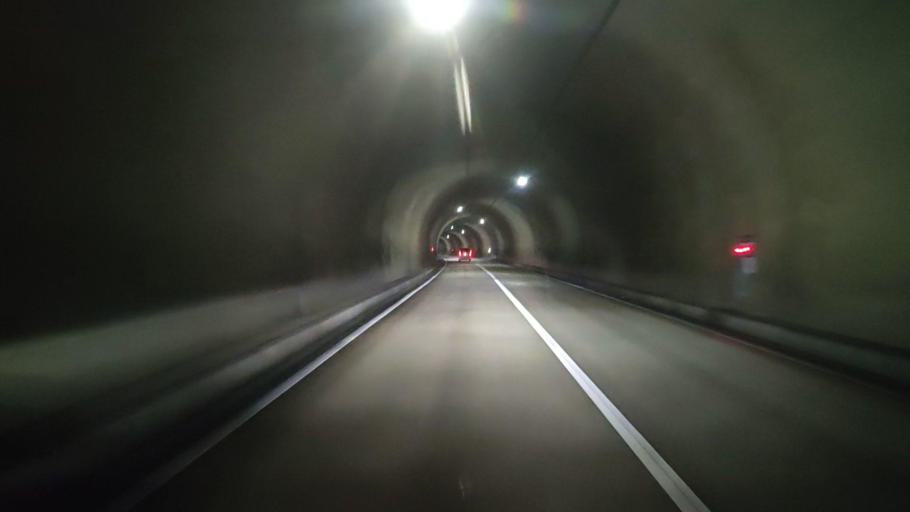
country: JP
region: Wakayama
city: Shingu
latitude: 33.8846
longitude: 135.8788
